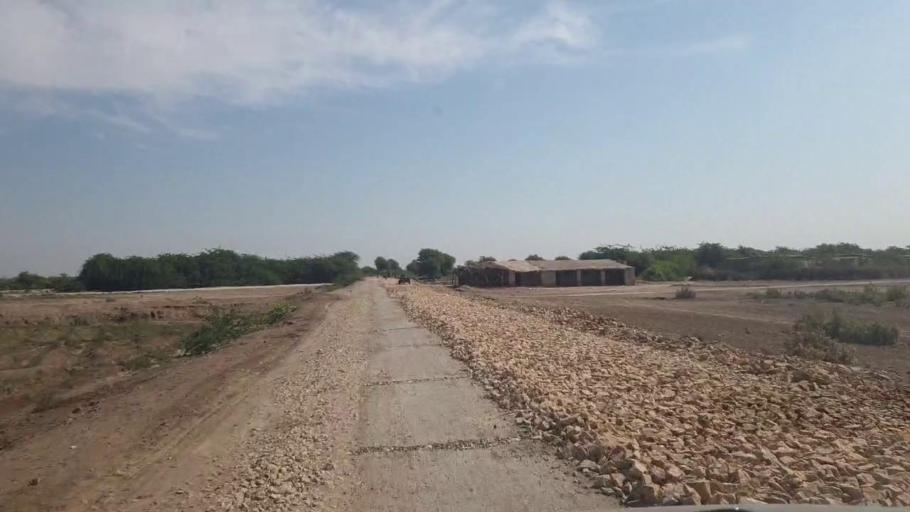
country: PK
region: Sindh
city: Tando Bago
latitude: 24.9426
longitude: 69.0990
